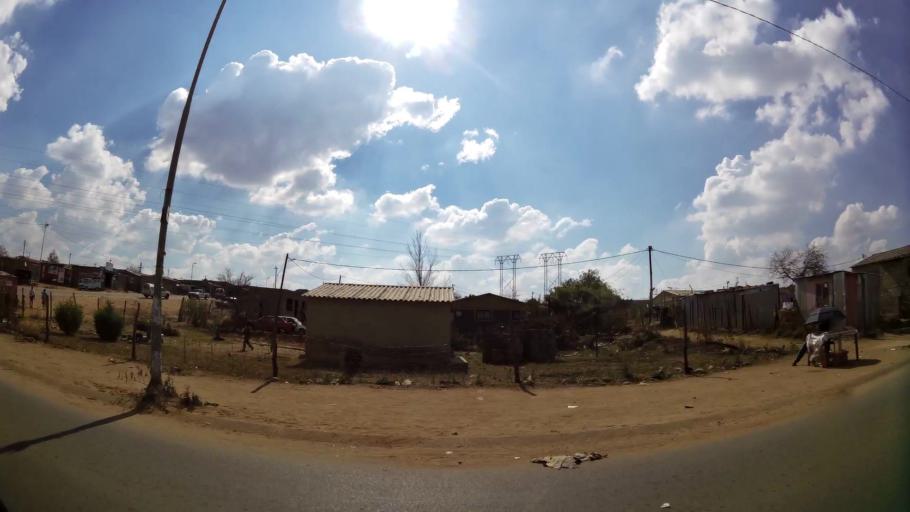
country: ZA
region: Gauteng
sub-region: City of Johannesburg Metropolitan Municipality
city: Roodepoort
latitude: -26.1899
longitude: 27.8653
